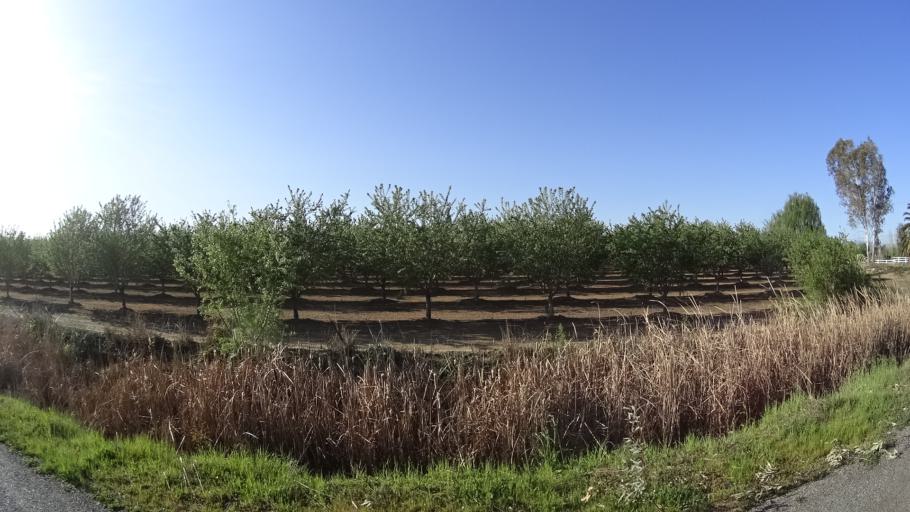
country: US
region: California
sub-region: Glenn County
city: Orland
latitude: 39.7977
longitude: -122.1496
